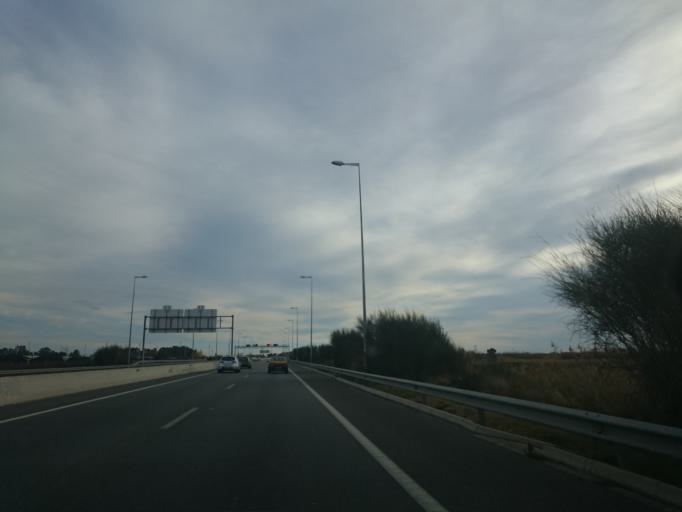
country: ES
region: Catalonia
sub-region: Provincia de Barcelona
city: Viladecans
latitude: 41.2921
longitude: 2.0507
